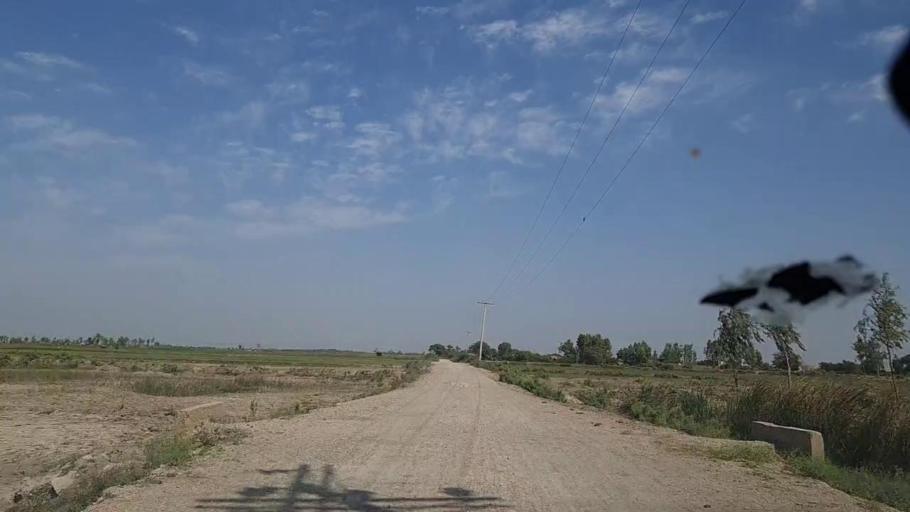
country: PK
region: Sindh
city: Daro Mehar
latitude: 24.6633
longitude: 68.0817
